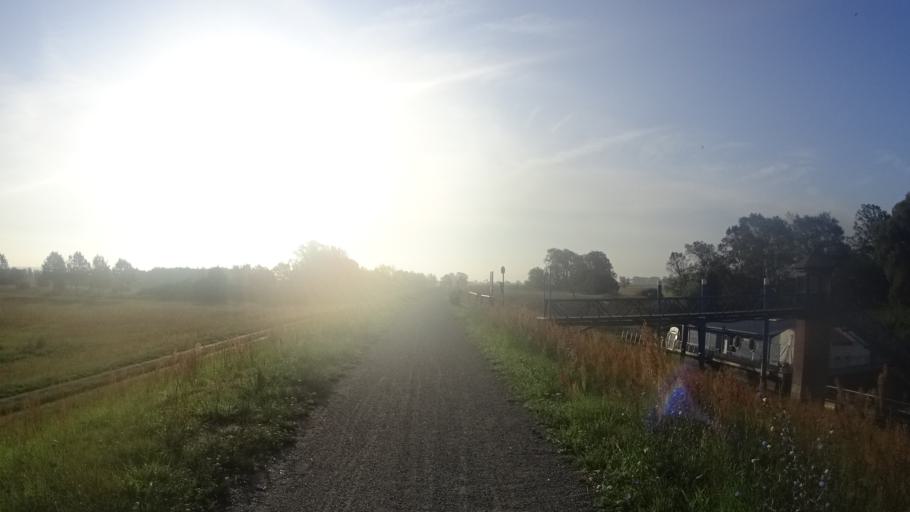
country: DE
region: Brandenburg
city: Lenzen
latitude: 53.0801
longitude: 11.4622
